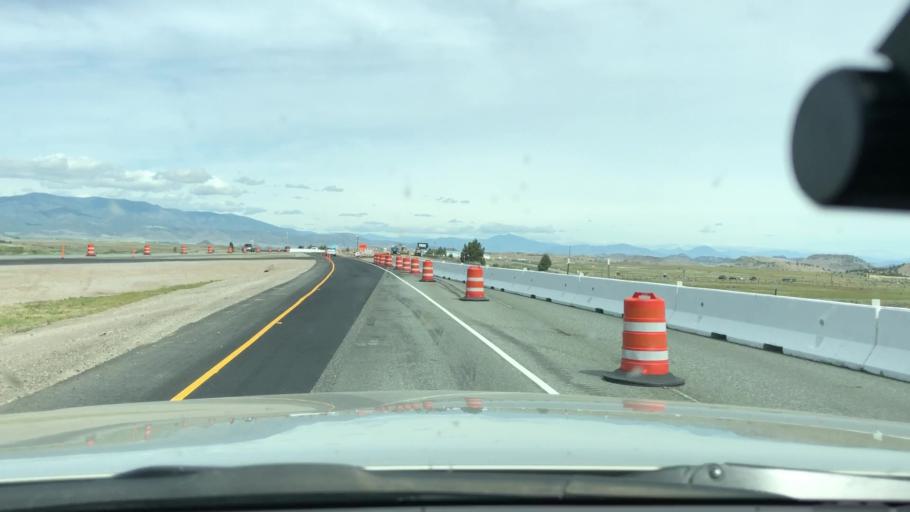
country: US
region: California
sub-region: Siskiyou County
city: Weed
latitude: 41.4685
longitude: -122.4496
